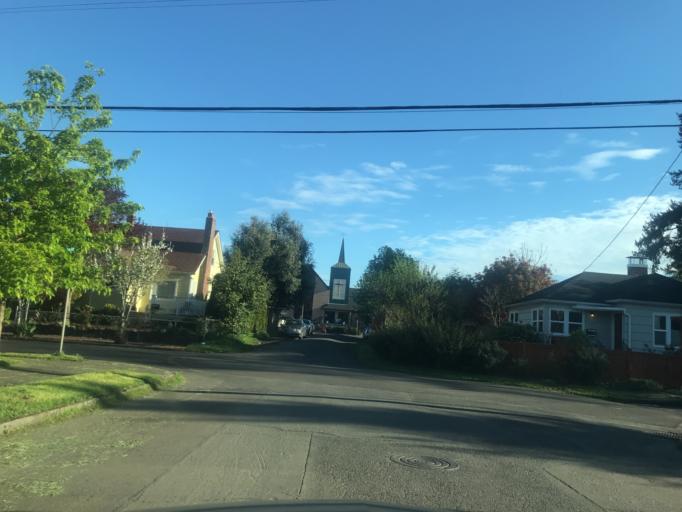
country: US
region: Oregon
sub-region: Multnomah County
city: Lents
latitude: 45.4952
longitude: -122.6054
